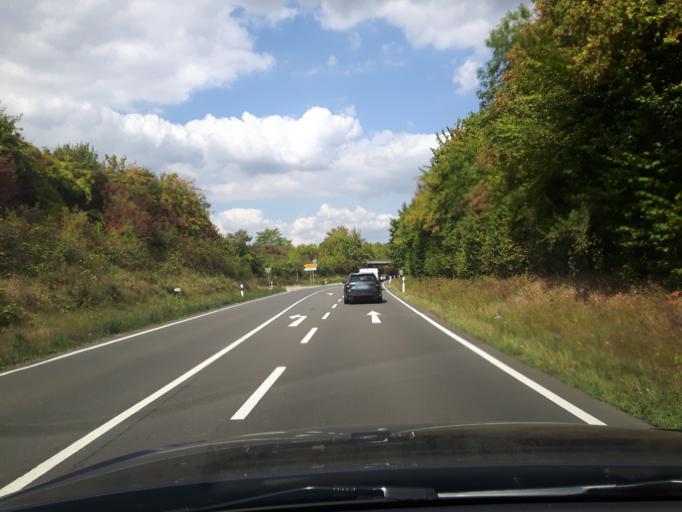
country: DE
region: Baden-Wuerttemberg
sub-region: Karlsruhe Region
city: Rauenberg
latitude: 49.2633
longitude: 8.7011
